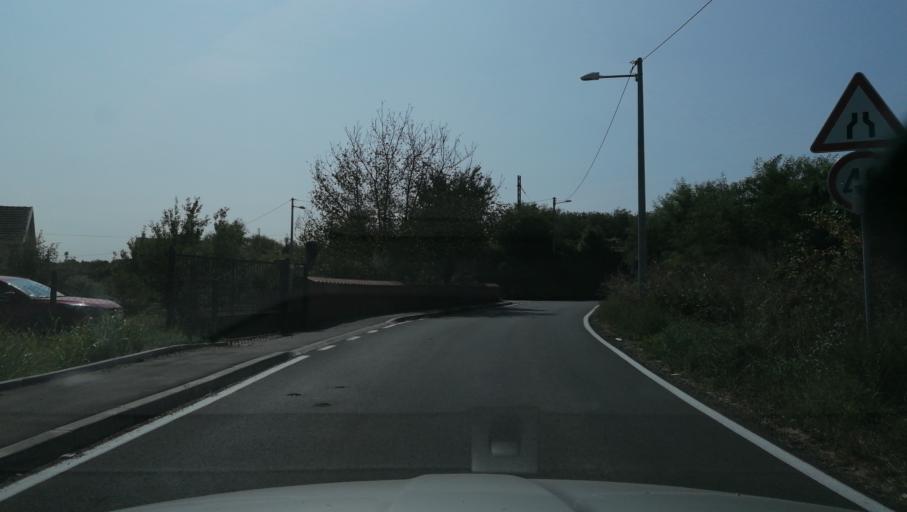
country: RS
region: Central Serbia
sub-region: Belgrade
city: Zvezdara
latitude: 44.7056
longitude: 20.5651
